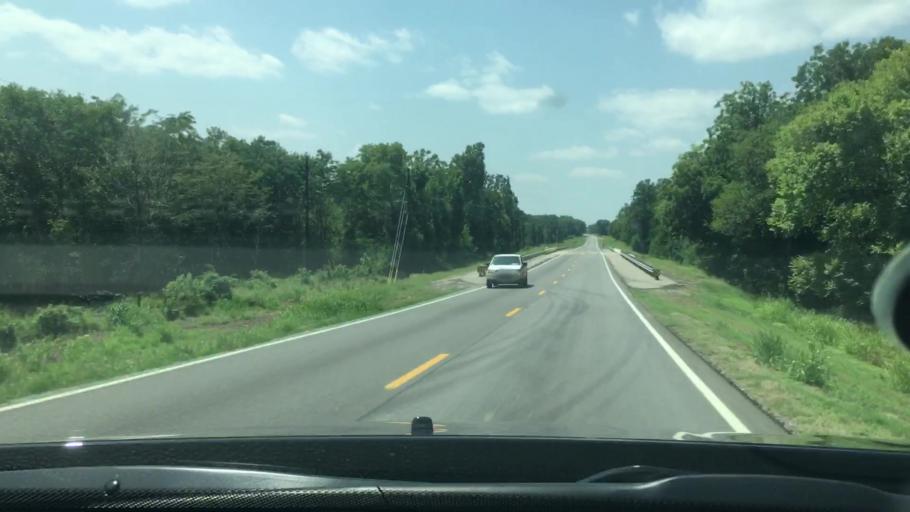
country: US
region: Oklahoma
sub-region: Atoka County
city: Atoka
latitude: 34.3791
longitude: -96.2772
